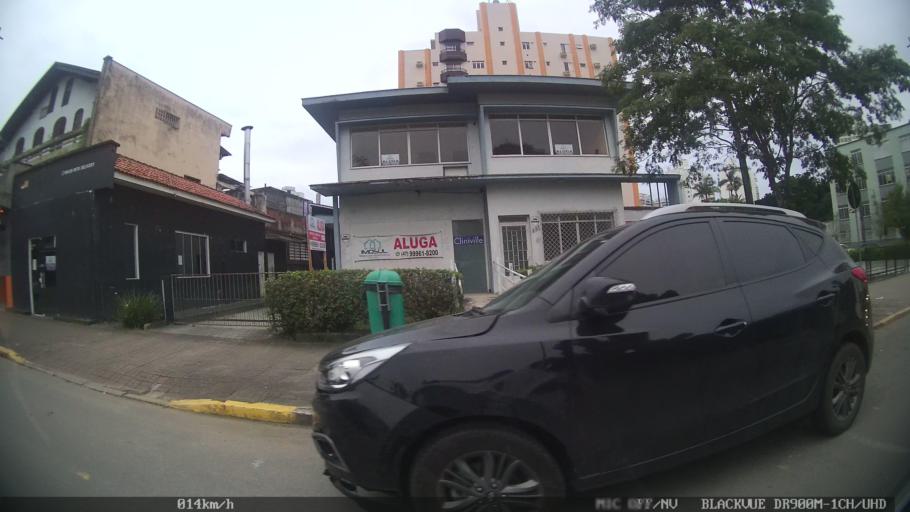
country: BR
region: Santa Catarina
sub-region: Joinville
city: Joinville
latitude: -26.3049
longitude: -48.8521
